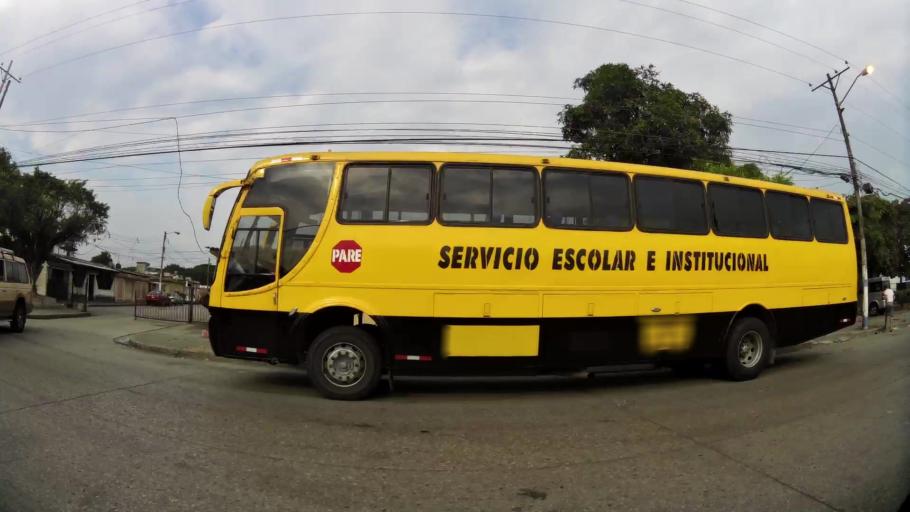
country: EC
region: Guayas
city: Guayaquil
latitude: -2.2489
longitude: -79.9031
